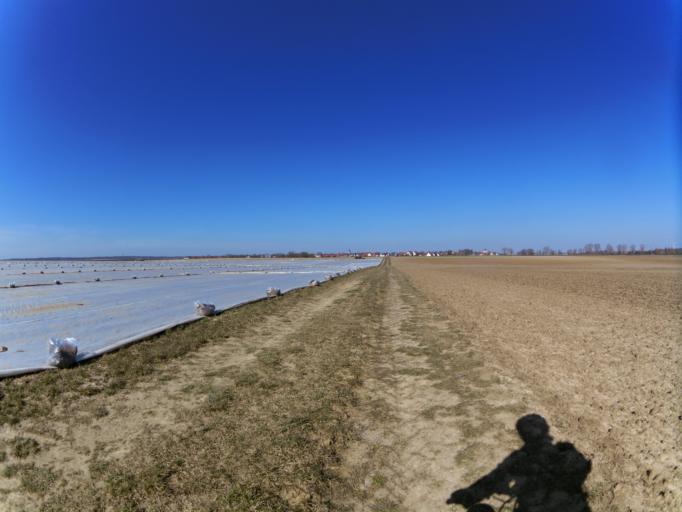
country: DE
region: Bavaria
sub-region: Regierungsbezirk Unterfranken
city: Oberpleichfeld
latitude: 49.8878
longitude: 10.0817
